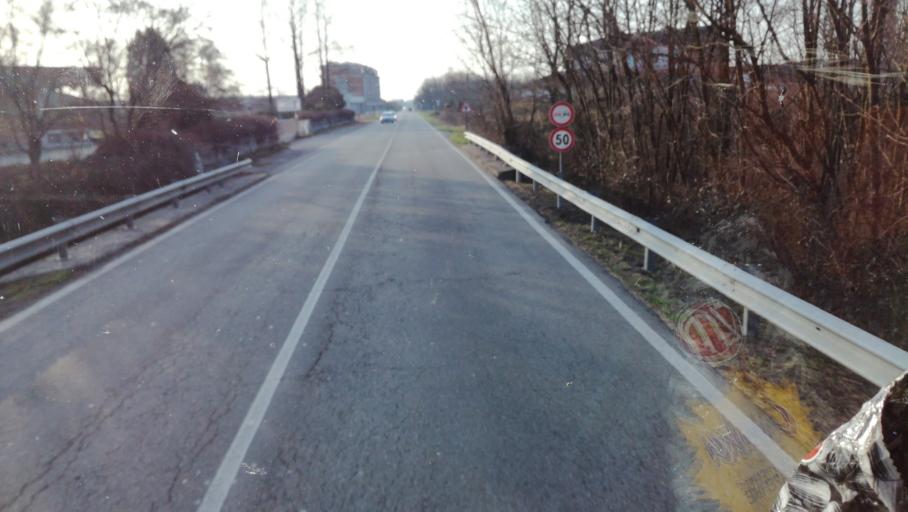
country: IT
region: Piedmont
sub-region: Provincia di Novara
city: Cressa
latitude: 45.6322
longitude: 8.5037
